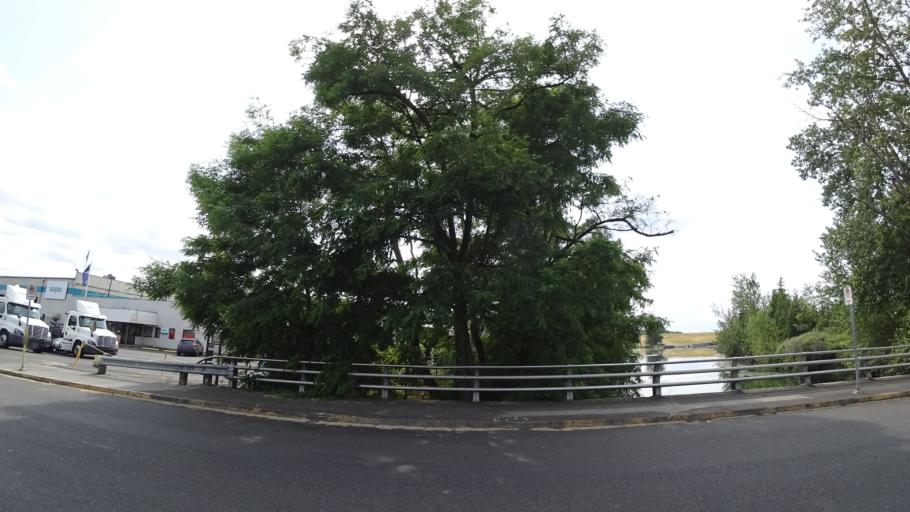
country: US
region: Washington
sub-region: Clark County
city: Vancouver
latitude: 45.5811
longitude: -122.6439
